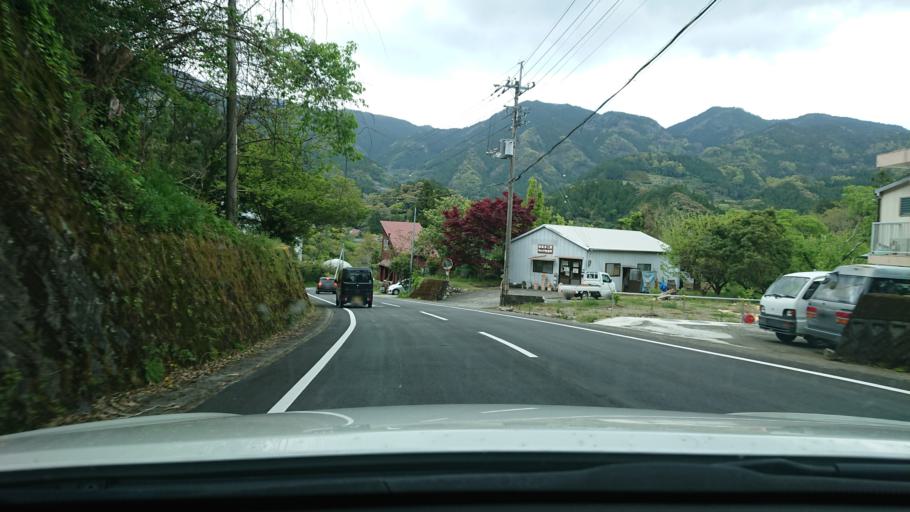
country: JP
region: Tokushima
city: Ishii
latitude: 33.9185
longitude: 134.4267
